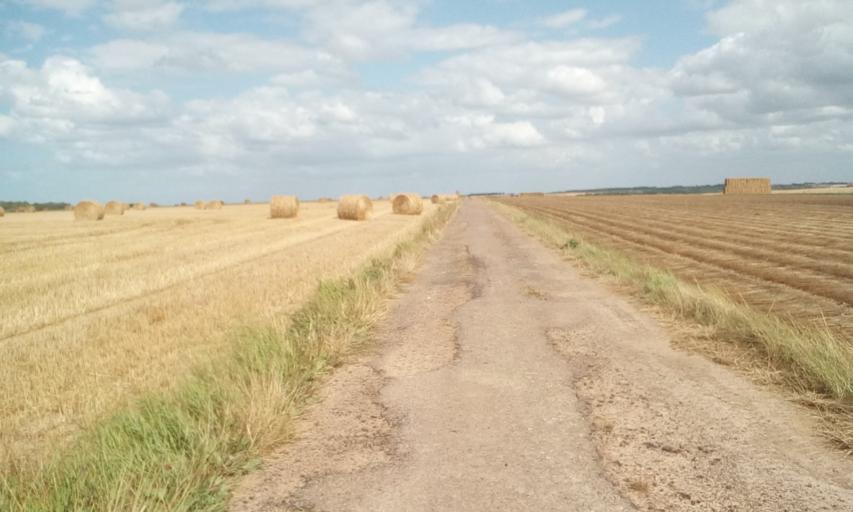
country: FR
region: Lower Normandy
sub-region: Departement du Calvados
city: Ver-sur-Mer
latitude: 49.3027
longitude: -0.5061
